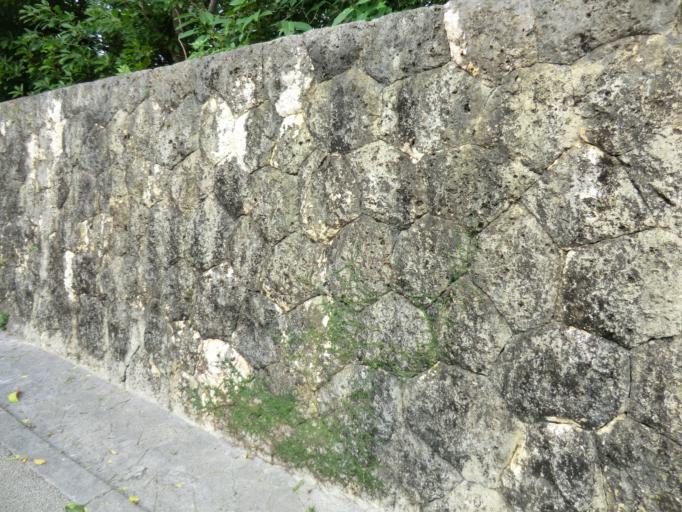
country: JP
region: Okinawa
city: Naha-shi
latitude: 26.2183
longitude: 127.7166
